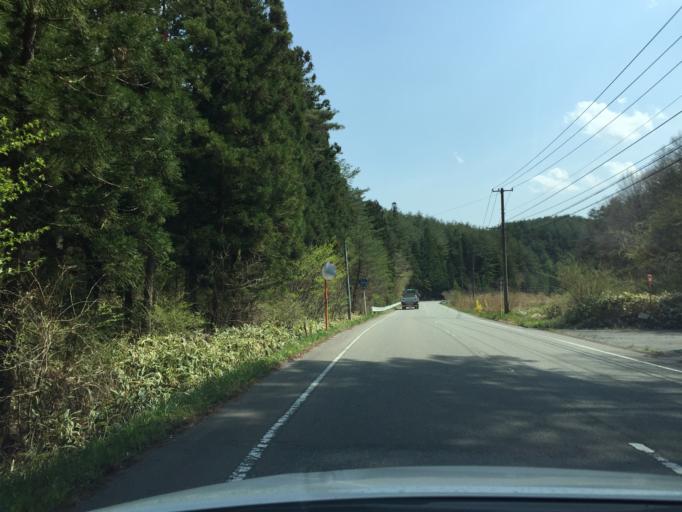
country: JP
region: Fukushima
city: Namie
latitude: 37.3742
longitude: 140.8022
